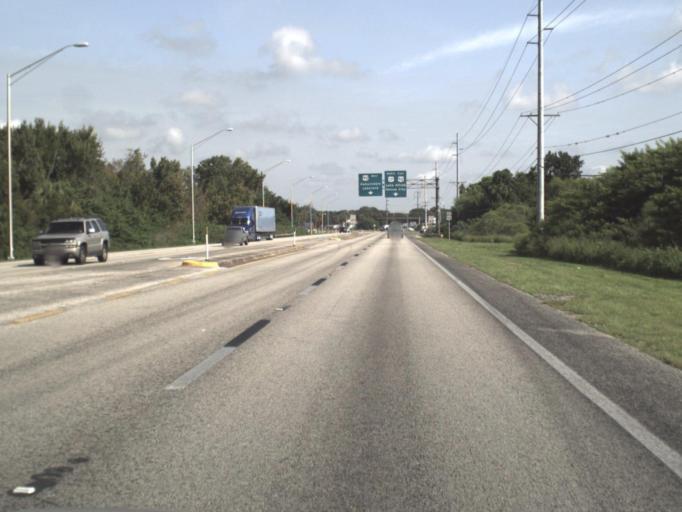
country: US
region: Florida
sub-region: Polk County
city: Lake Alfred
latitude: 28.0709
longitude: -81.7326
